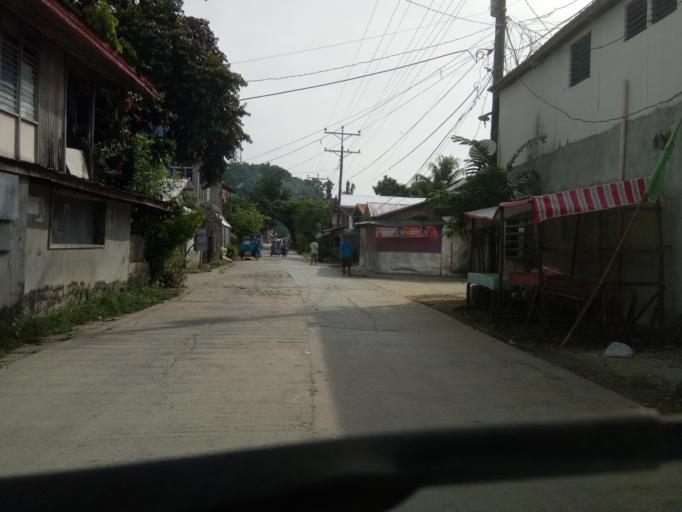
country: PH
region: Caraga
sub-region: Province of Surigao del Norte
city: Dapa
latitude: 9.7563
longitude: 126.0523
